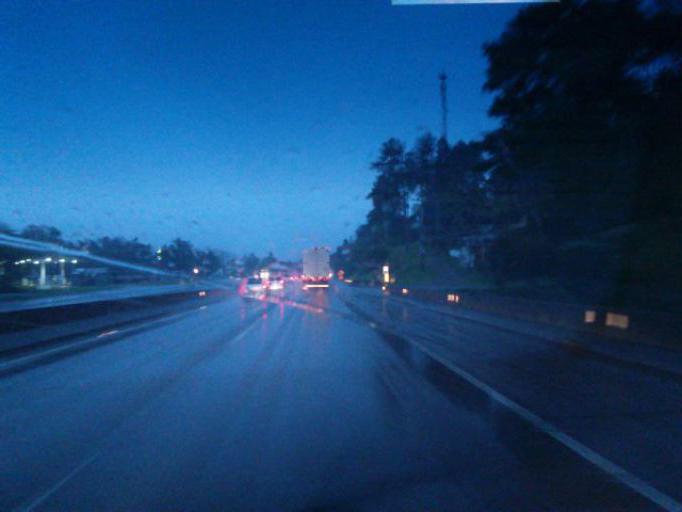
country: BR
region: Sao Paulo
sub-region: Juquitiba
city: Juquitiba
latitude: -23.9368
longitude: -47.0359
